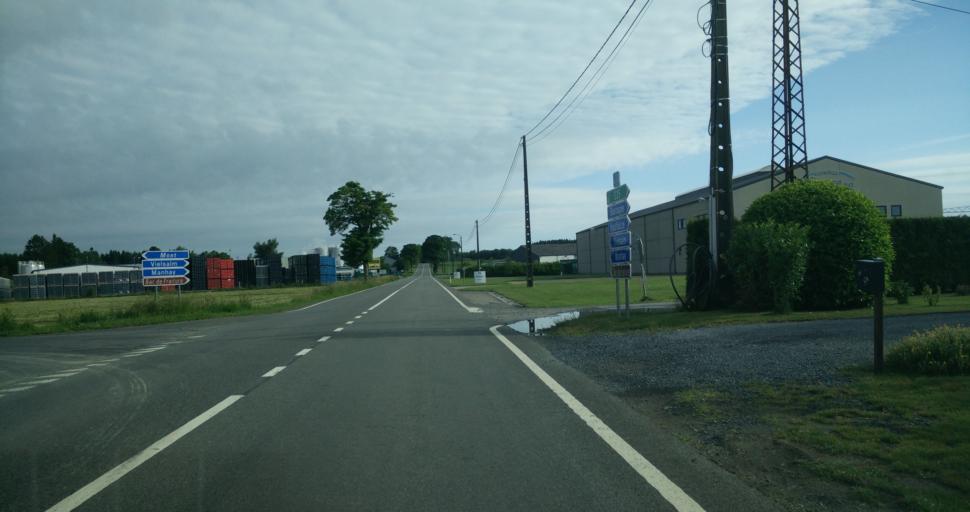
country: BE
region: Wallonia
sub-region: Province du Luxembourg
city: Houffalize
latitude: 50.1580
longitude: 5.7832
